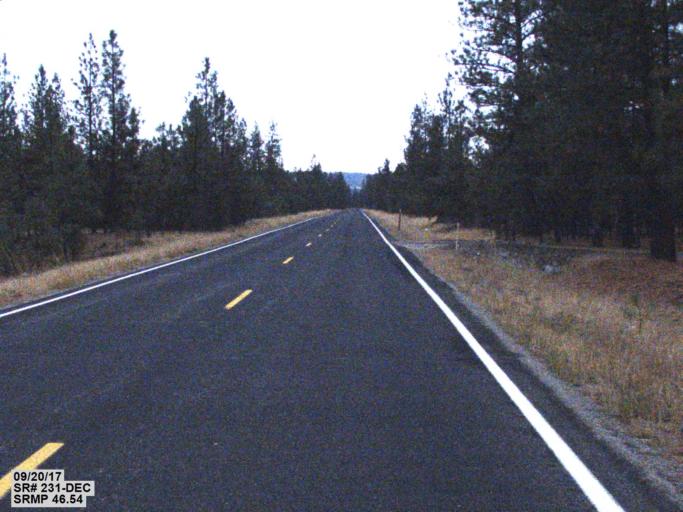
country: US
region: Washington
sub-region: Spokane County
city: Fairchild Air Force Base
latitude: 47.8621
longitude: -117.8440
